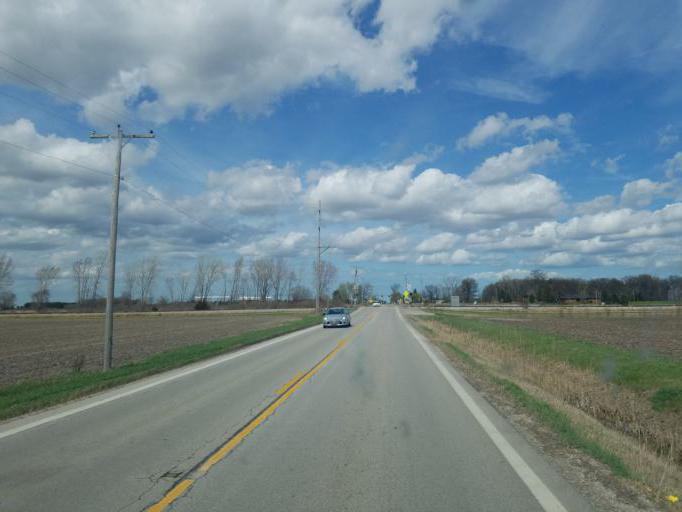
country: US
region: Ohio
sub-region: Huron County
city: Bellevue
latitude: 41.2620
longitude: -82.7963
